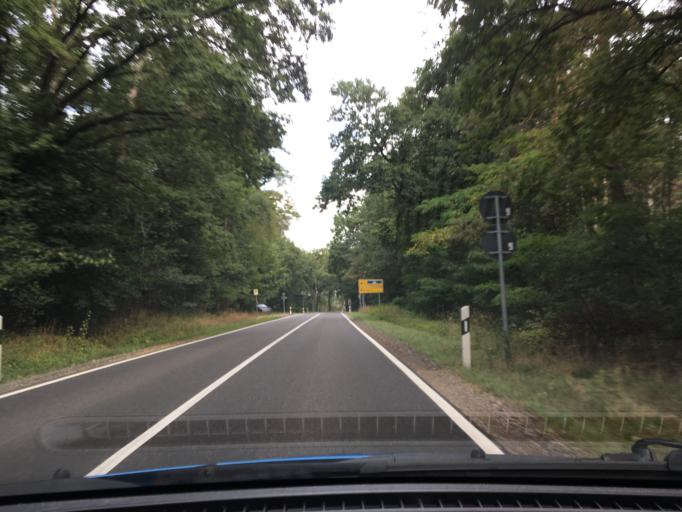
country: DE
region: Mecklenburg-Vorpommern
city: Neu Kaliss
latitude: 53.2002
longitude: 11.3024
